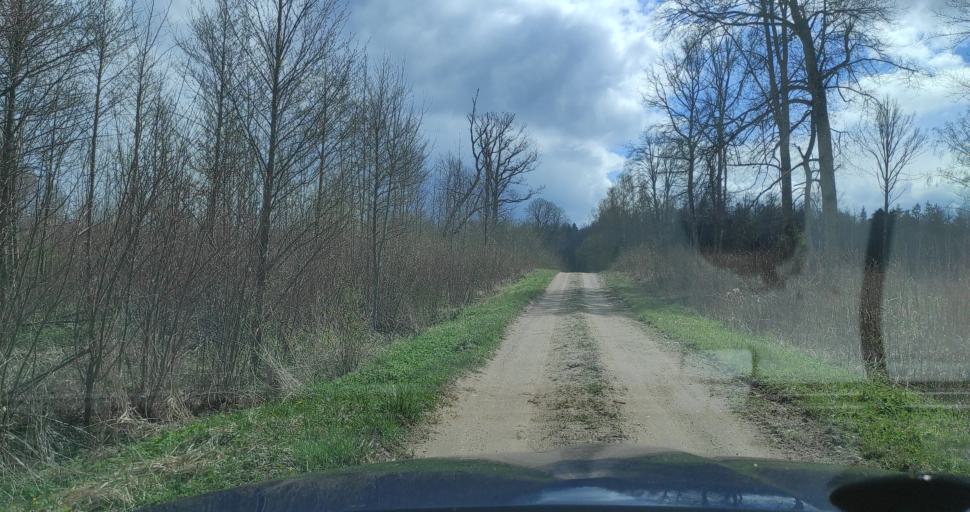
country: LV
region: Kuldigas Rajons
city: Kuldiga
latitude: 56.8661
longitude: 21.8279
